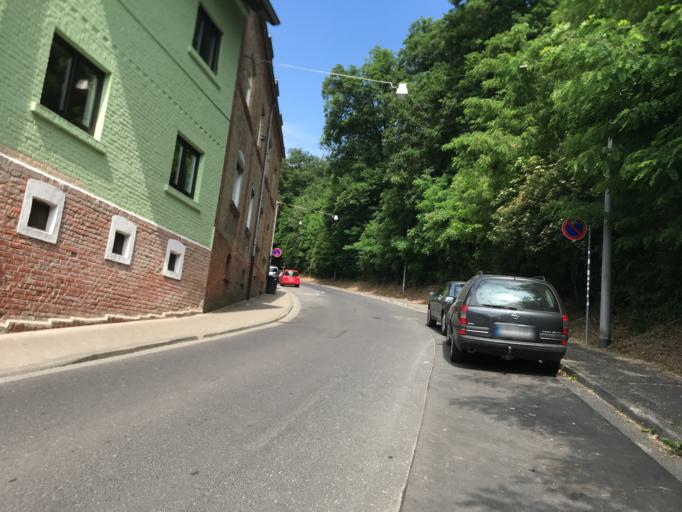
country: DE
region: Hesse
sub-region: Regierungsbezirk Darmstadt
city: Walluf
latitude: 50.0747
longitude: 8.1857
